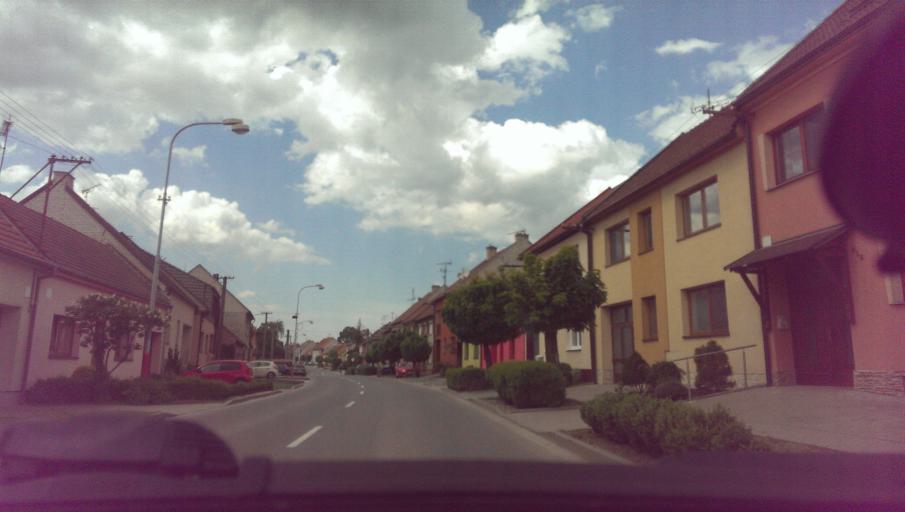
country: CZ
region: Zlin
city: Dolni Nemci
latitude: 48.9689
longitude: 17.5961
